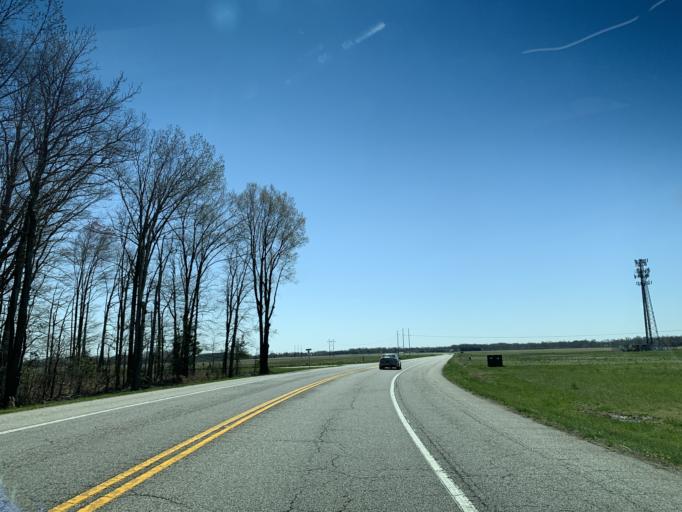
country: US
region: Maryland
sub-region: Caroline County
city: Ridgely
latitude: 38.9379
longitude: -75.9691
